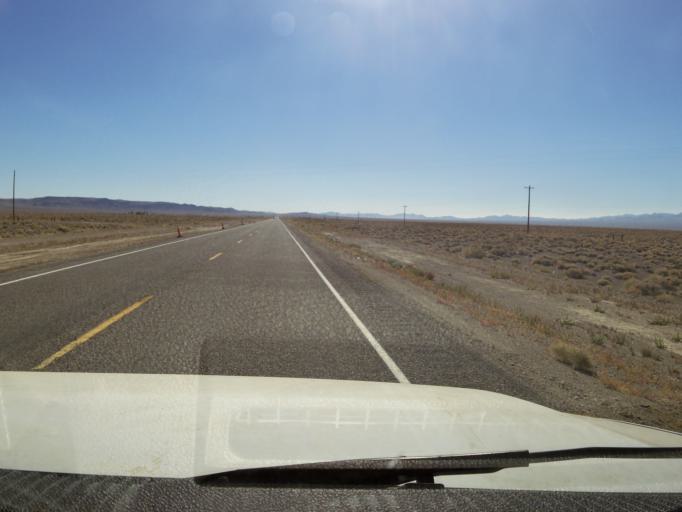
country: US
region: Nevada
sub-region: Esmeralda County
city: Goldfield
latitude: 37.2935
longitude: -117.0480
